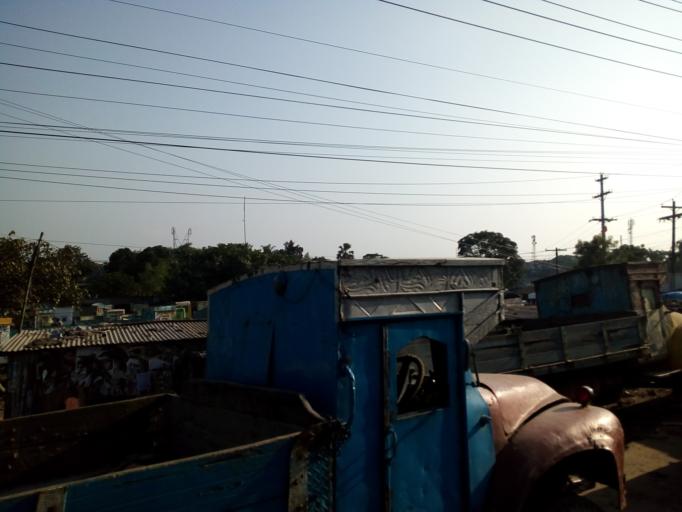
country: BD
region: Dhaka
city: Tungi
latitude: 23.9123
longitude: 90.2334
